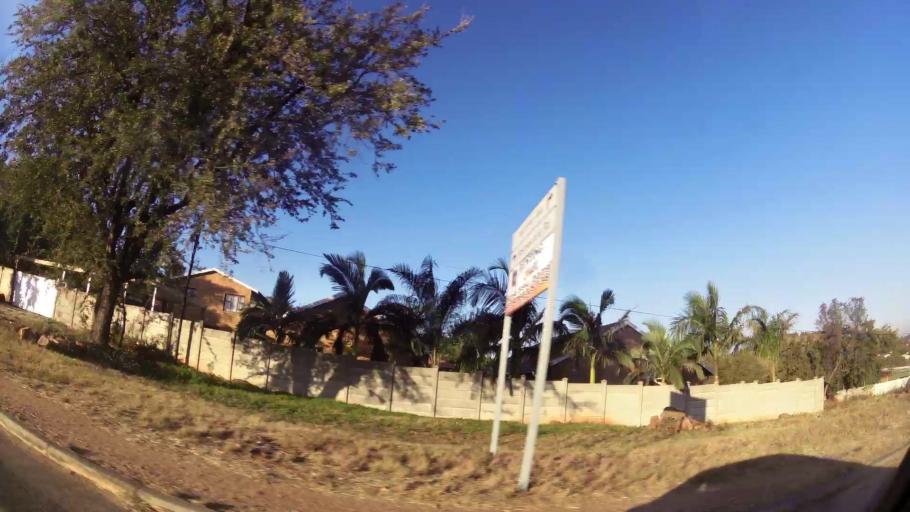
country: ZA
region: North-West
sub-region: Bojanala Platinum District Municipality
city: Rustenburg
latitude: -25.7075
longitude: 27.2398
